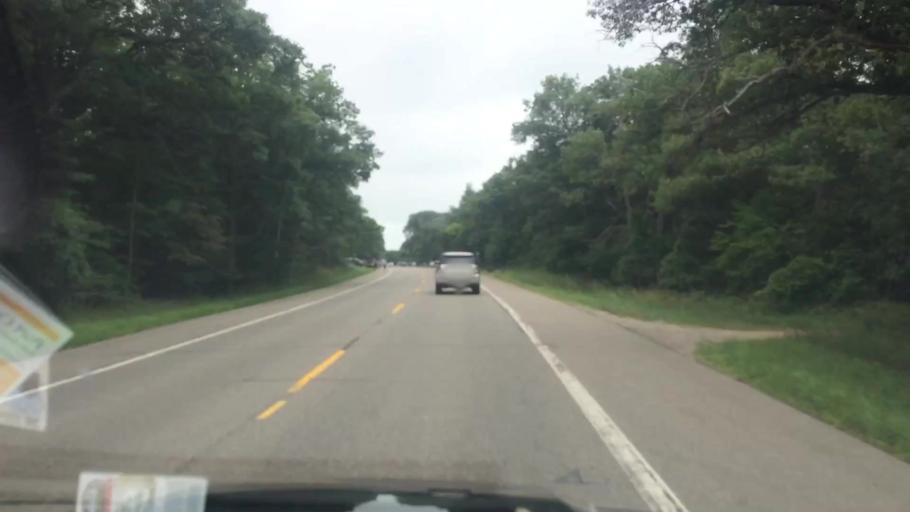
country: US
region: Michigan
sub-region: Huron County
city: Pigeon
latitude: 43.9789
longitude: -83.2339
